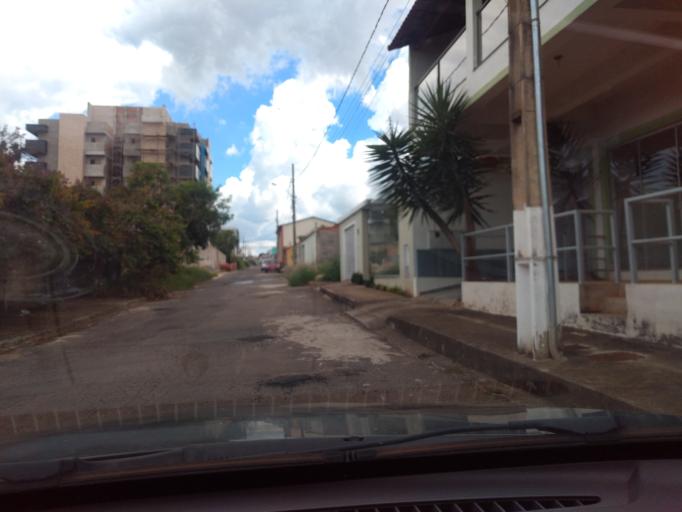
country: BR
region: Minas Gerais
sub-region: Tres Coracoes
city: Tres Coracoes
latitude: -21.6782
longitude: -45.2692
